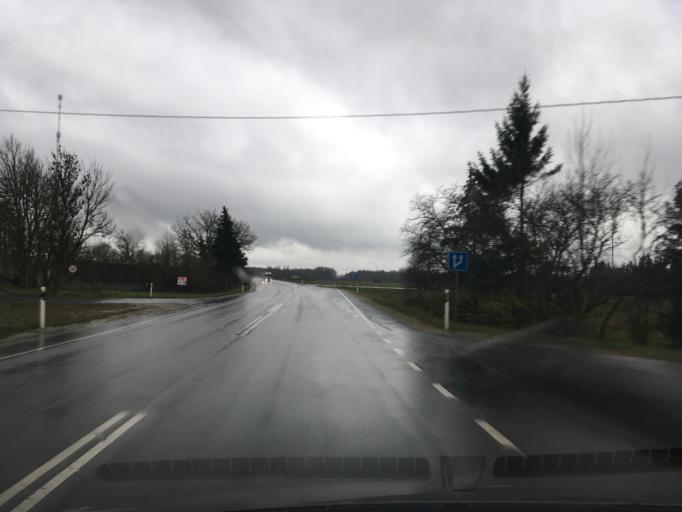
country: EE
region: Laeaene
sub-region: Lihula vald
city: Lihula
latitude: 58.7678
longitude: 23.9882
